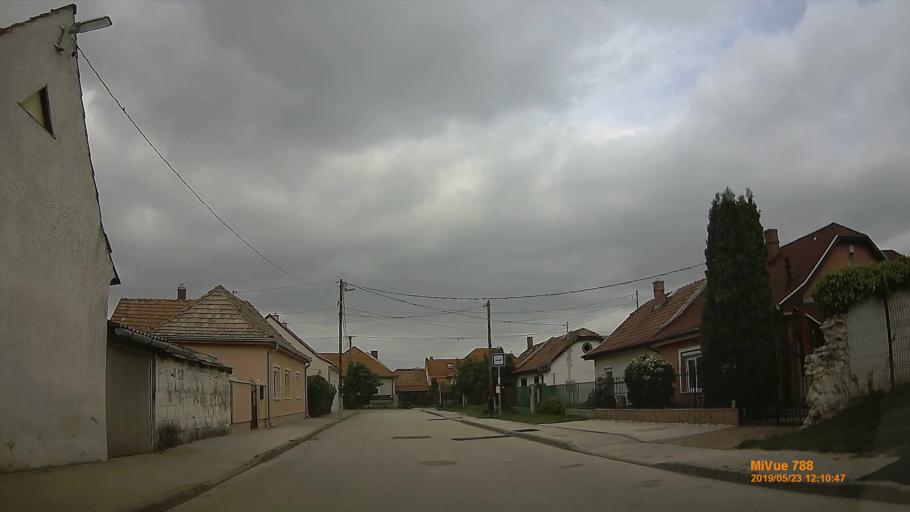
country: HU
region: Veszprem
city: Veszprem
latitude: 47.1018
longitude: 17.9037
